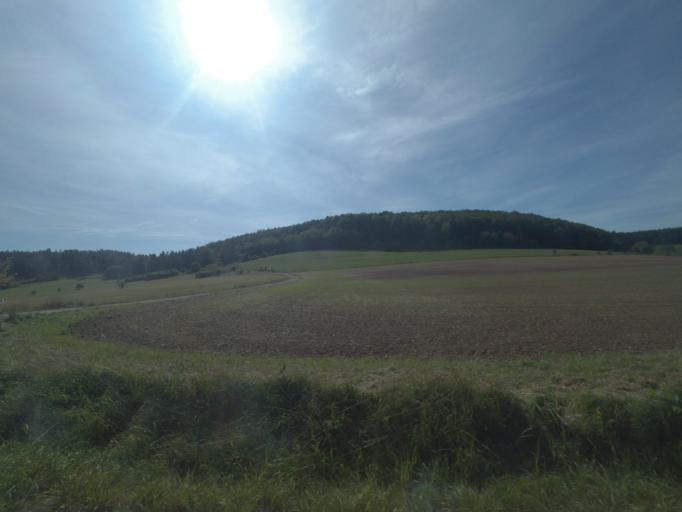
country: DE
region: Thuringia
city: Metzels
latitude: 50.6429
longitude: 10.4602
